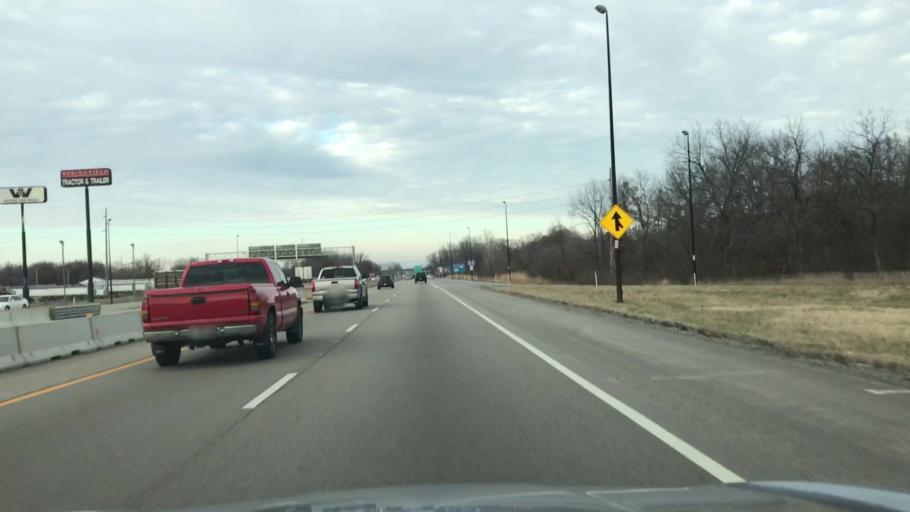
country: US
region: Illinois
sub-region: Sangamon County
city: Grandview
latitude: 39.7889
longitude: -89.5985
